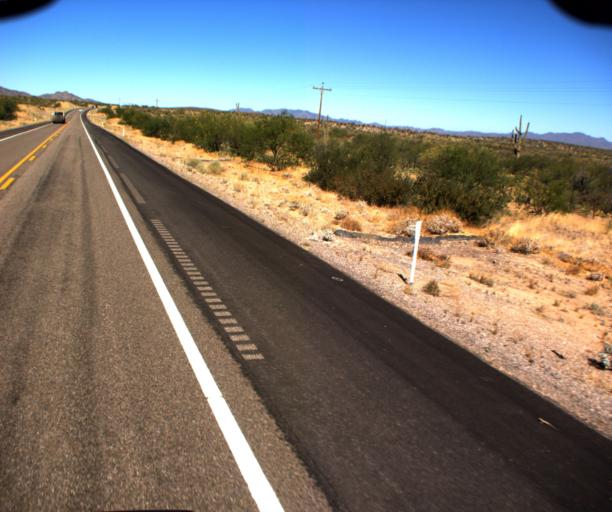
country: US
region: Arizona
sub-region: Pima County
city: Three Points
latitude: 32.0307
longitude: -111.5608
